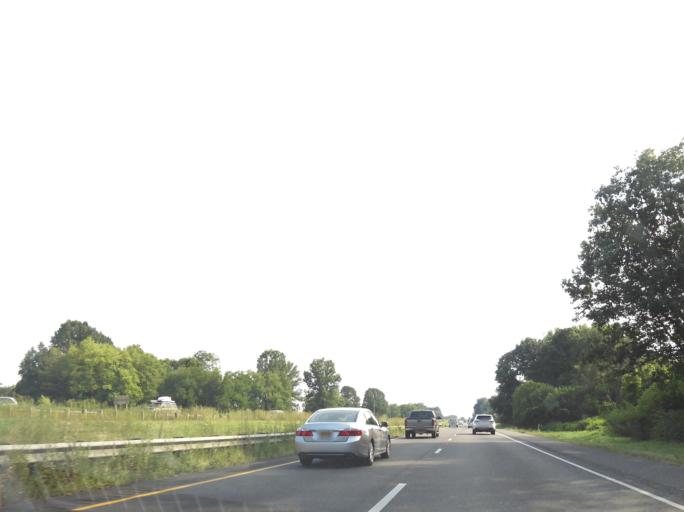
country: US
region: Maryland
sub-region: Washington County
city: Williamsport
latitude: 39.6054
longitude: -77.8034
